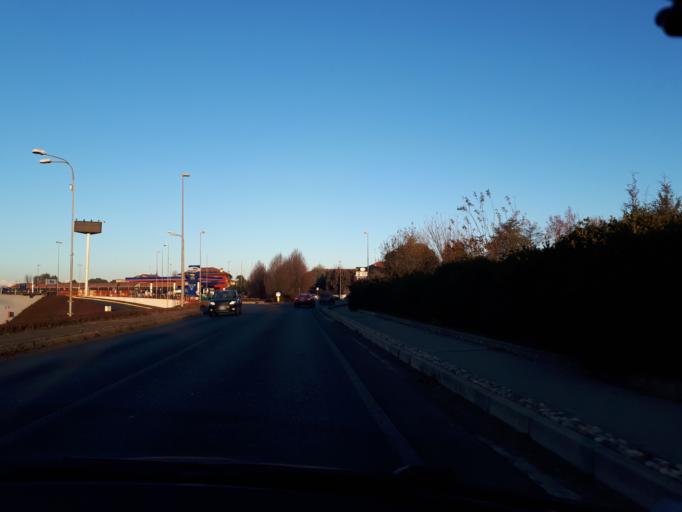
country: IT
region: Lombardy
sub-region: Provincia di Como
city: Vertemate Con Minoprio
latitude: 45.7162
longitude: 9.0773
